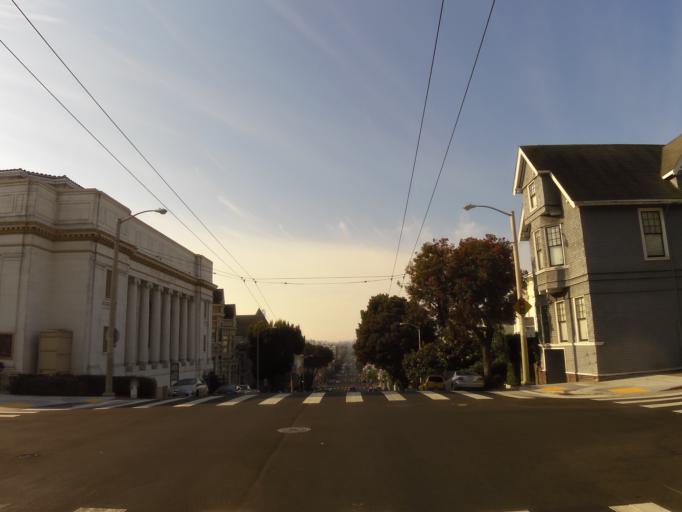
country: US
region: California
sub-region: San Francisco County
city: San Francisco
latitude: 37.7900
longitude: -122.4409
